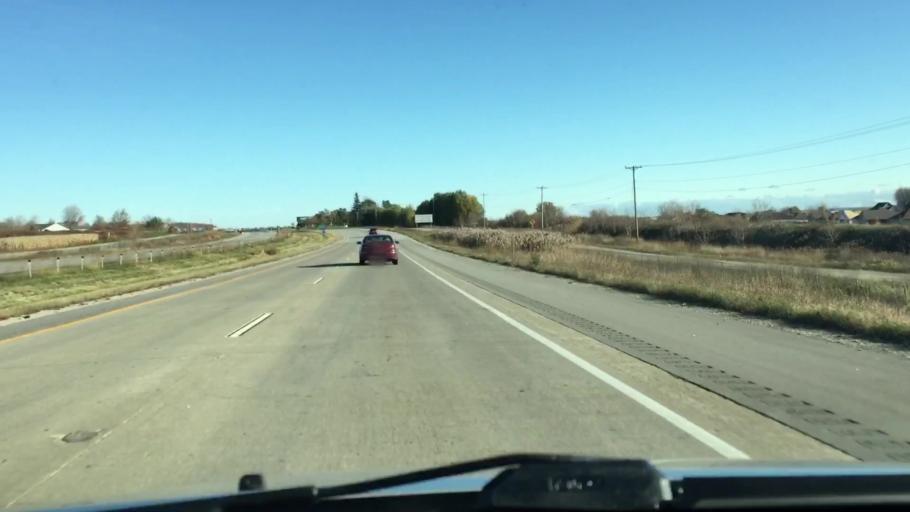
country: US
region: Wisconsin
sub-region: Brown County
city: Wrightstown
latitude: 44.3299
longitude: -88.2093
